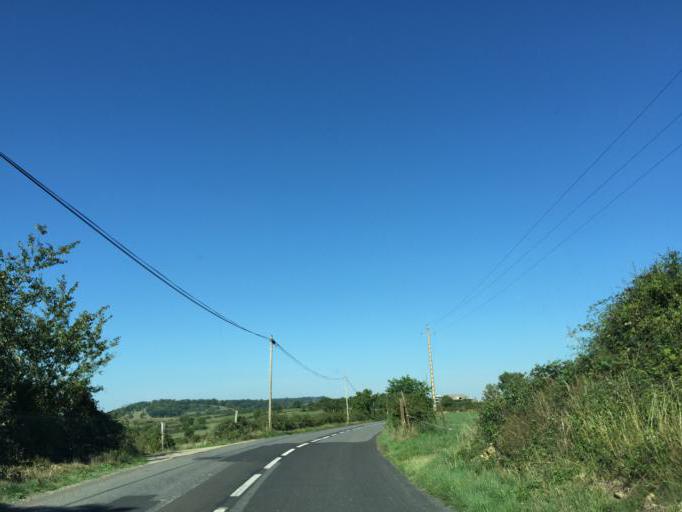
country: FR
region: Midi-Pyrenees
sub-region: Departement de l'Aveyron
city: Espalion
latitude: 44.4914
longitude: 2.7558
